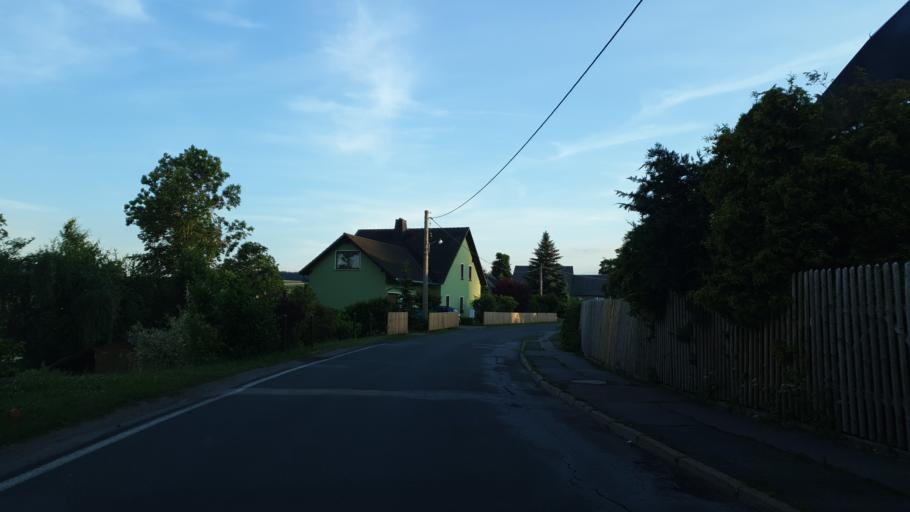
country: DE
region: Saxony
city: Stollberg
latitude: 50.6927
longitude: 12.7635
